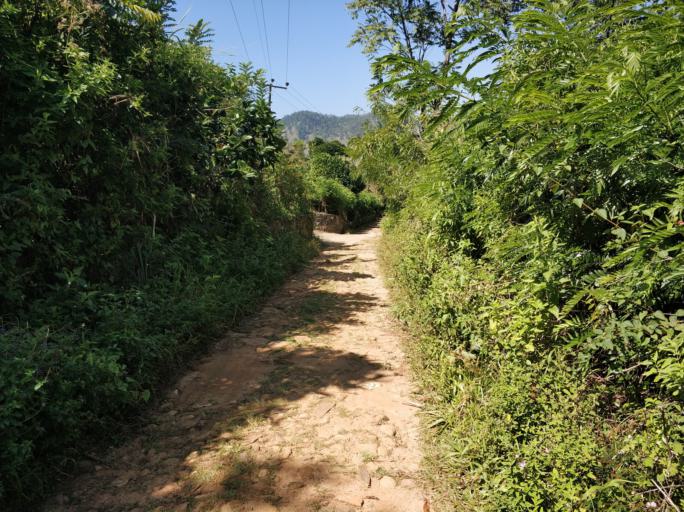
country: LK
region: Uva
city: Haputale
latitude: 6.8323
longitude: 81.0572
